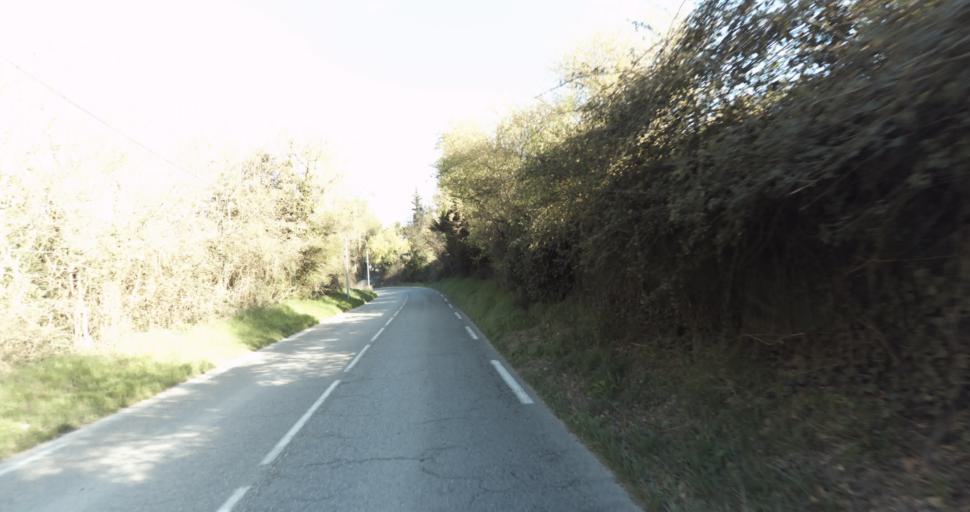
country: FR
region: Provence-Alpes-Cote d'Azur
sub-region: Departement des Bouches-du-Rhone
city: Aix-en-Provence
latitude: 43.5608
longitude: 5.4316
